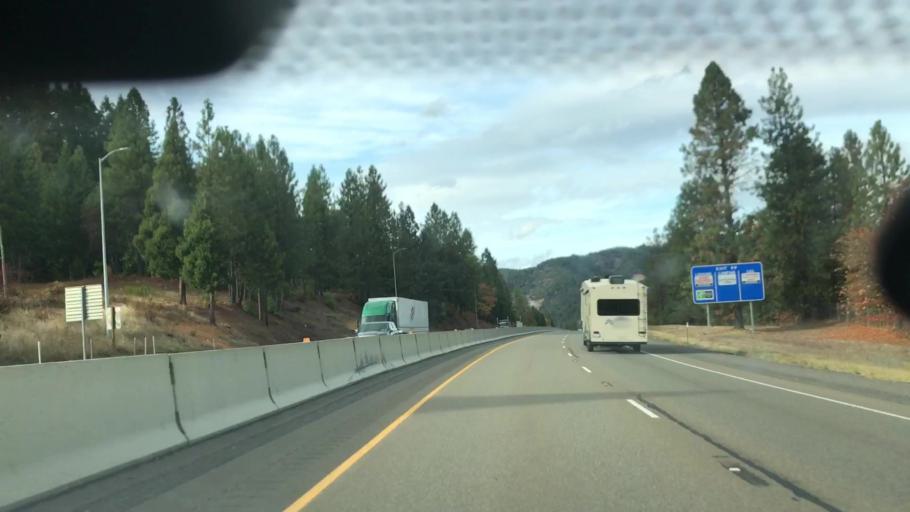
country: US
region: Oregon
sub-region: Douglas County
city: Canyonville
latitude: 42.9291
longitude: -123.2825
